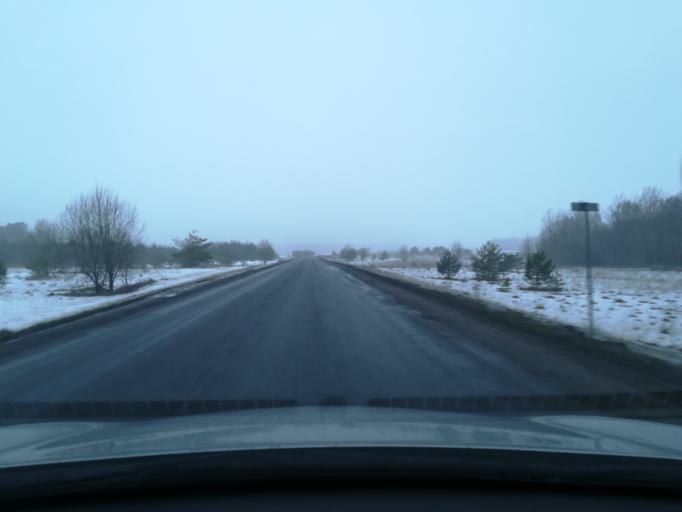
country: EE
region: Harju
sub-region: Raasiku vald
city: Arukula
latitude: 59.3485
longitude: 25.0936
